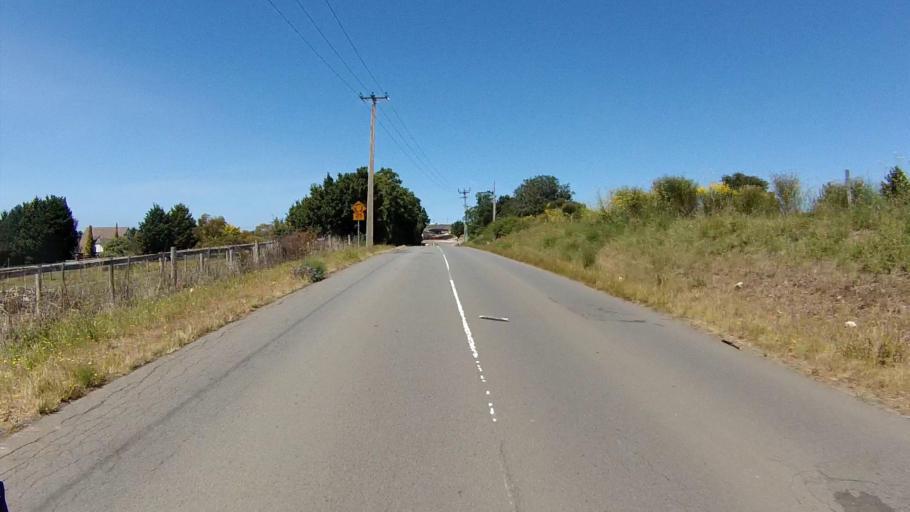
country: AU
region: Tasmania
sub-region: Clarence
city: Howrah
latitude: -42.8821
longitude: 147.4280
